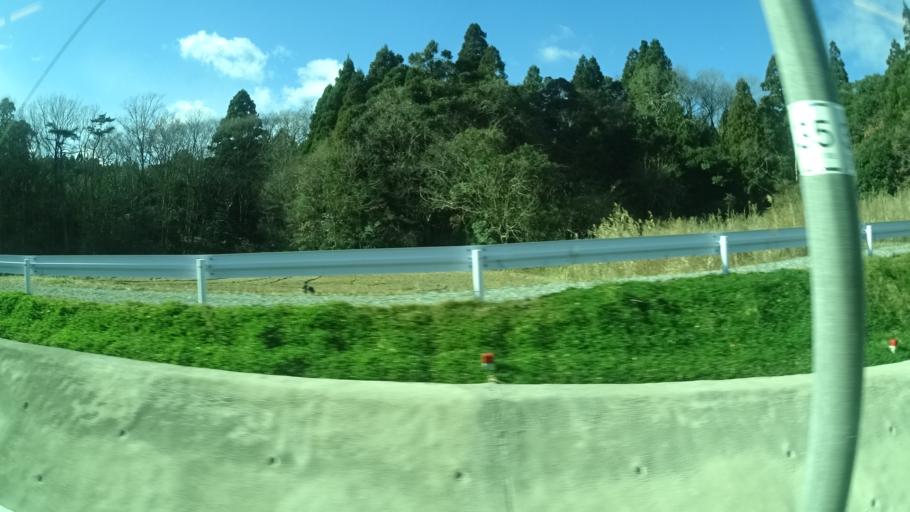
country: JP
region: Miyagi
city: Marumori
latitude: 37.8962
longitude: 140.9188
